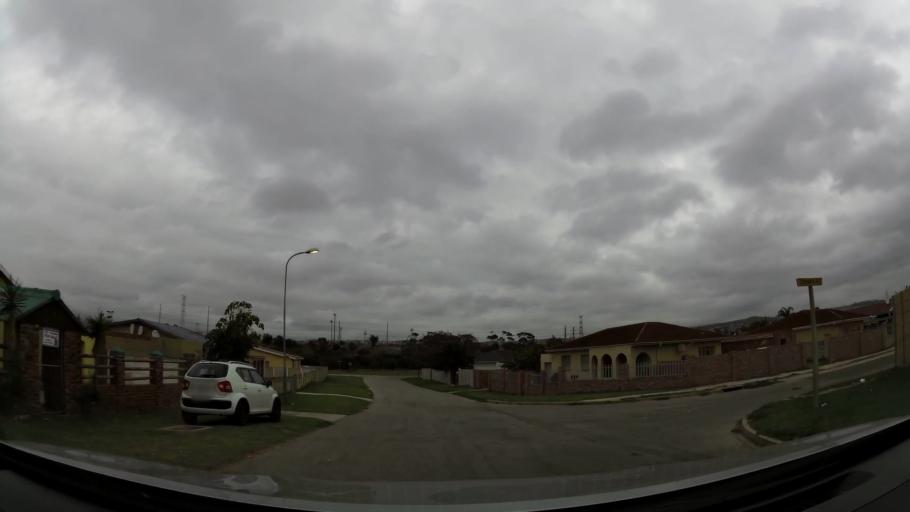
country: ZA
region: Eastern Cape
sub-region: Nelson Mandela Bay Metropolitan Municipality
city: Port Elizabeth
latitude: -33.9075
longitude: 25.5645
